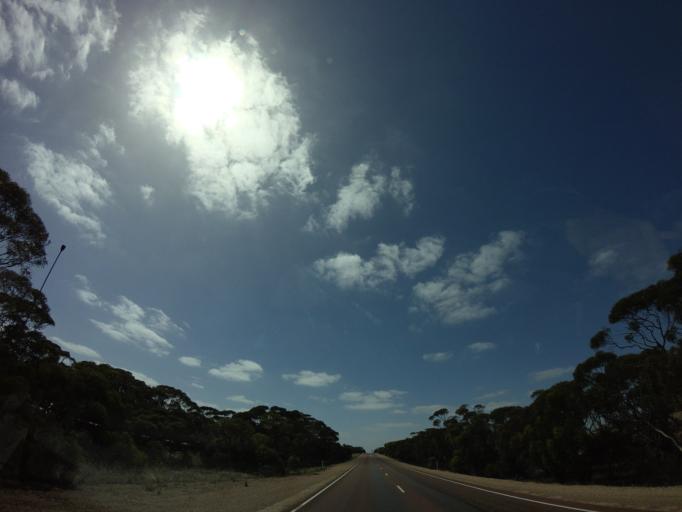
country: AU
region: South Australia
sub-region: Kimba
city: Caralue
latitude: -33.1219
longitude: 135.5422
